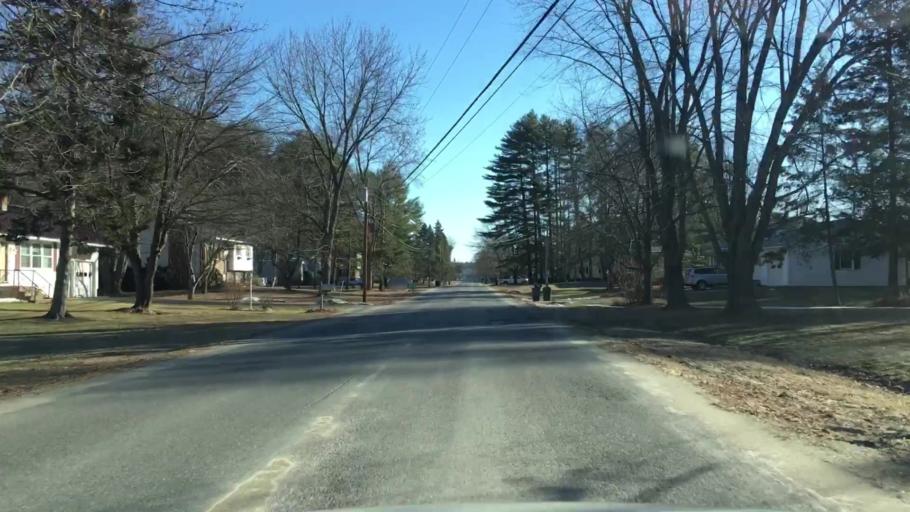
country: US
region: Maine
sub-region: Kennebec County
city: Winslow
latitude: 44.5491
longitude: -69.6043
